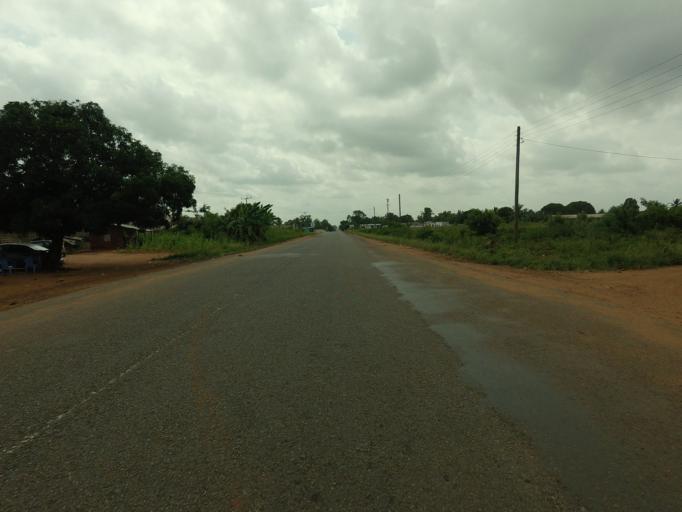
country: TG
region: Maritime
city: Lome
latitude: 6.1369
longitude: 1.1158
